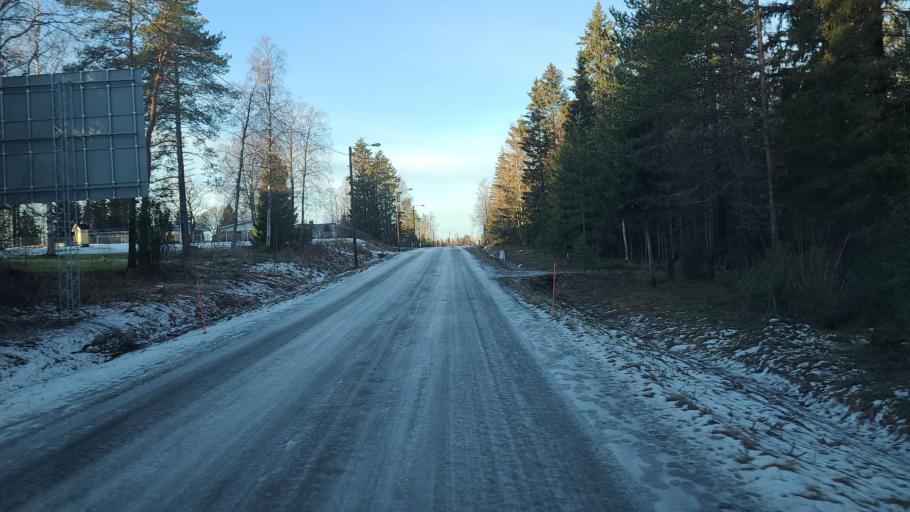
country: FI
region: Lapland
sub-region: Kemi-Tornio
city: Kemi
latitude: 65.6805
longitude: 24.7387
